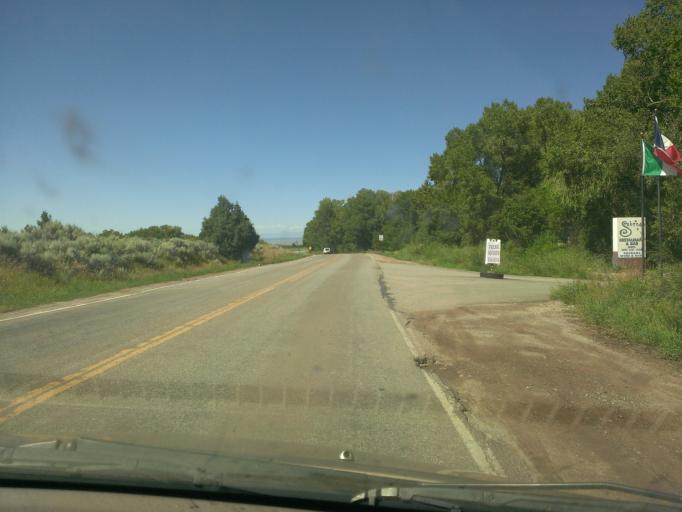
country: US
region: New Mexico
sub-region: Taos County
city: Arroyo Seco
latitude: 36.5150
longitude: -105.5713
